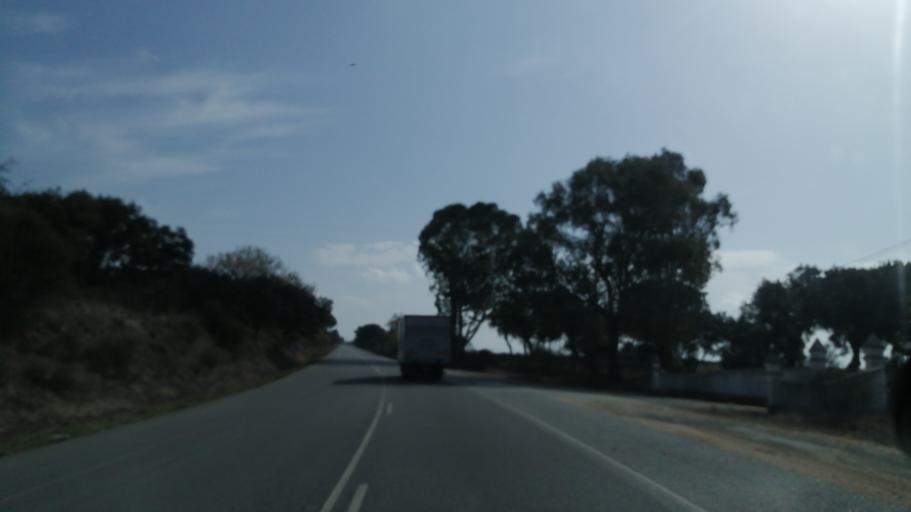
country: PT
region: Evora
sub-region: Montemor-O-Novo
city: Montemor-o-Novo
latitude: 38.6268
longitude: -8.1078
